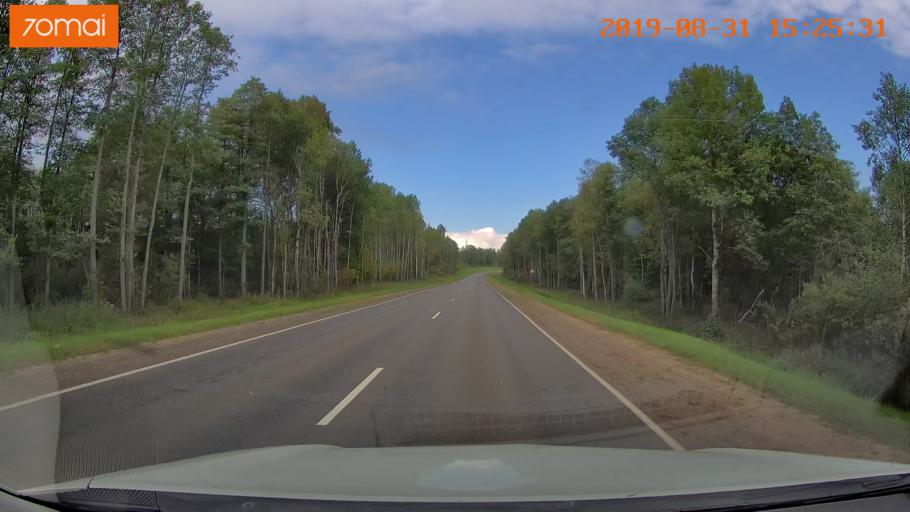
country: RU
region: Kaluga
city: Baryatino
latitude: 54.5424
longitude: 34.5207
